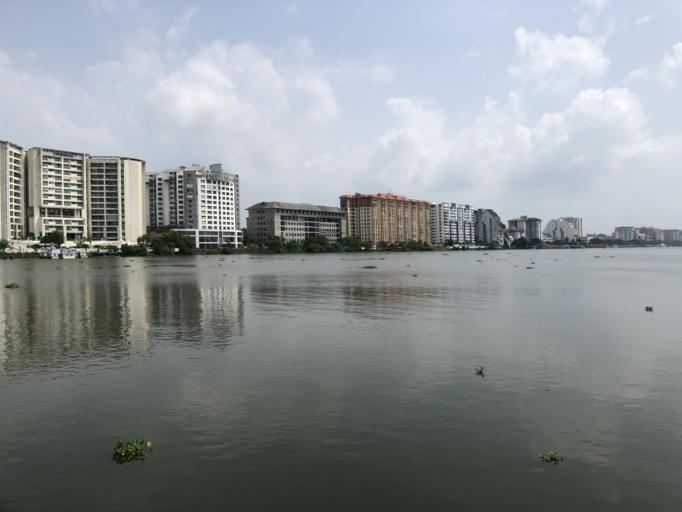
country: IN
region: Kerala
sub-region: Ernakulam
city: Cochin
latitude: 9.9900
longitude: 76.2674
